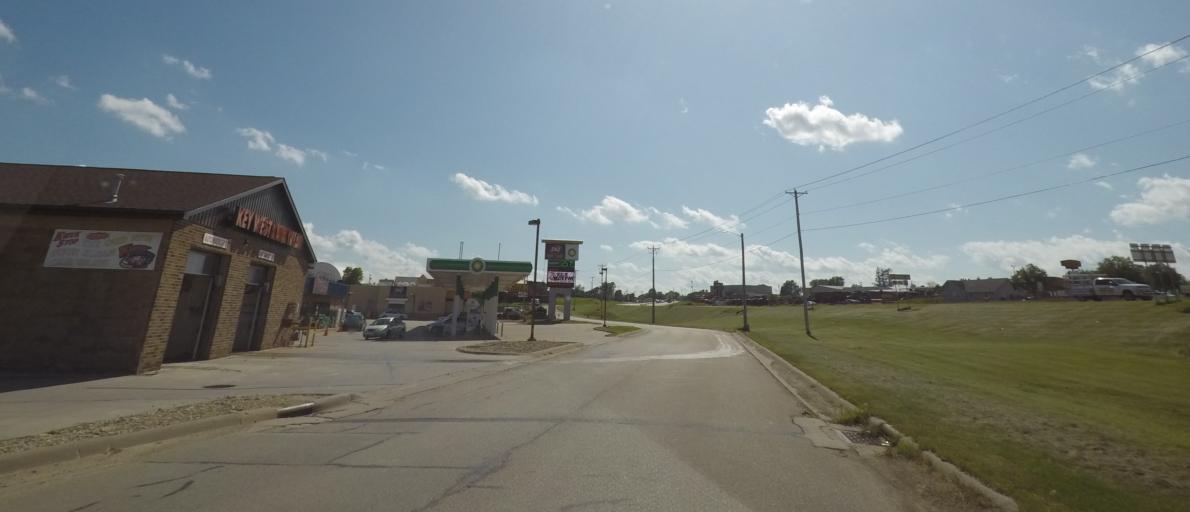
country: US
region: Iowa
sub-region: Dubuque County
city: Dubuque
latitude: 42.4589
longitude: -90.6724
